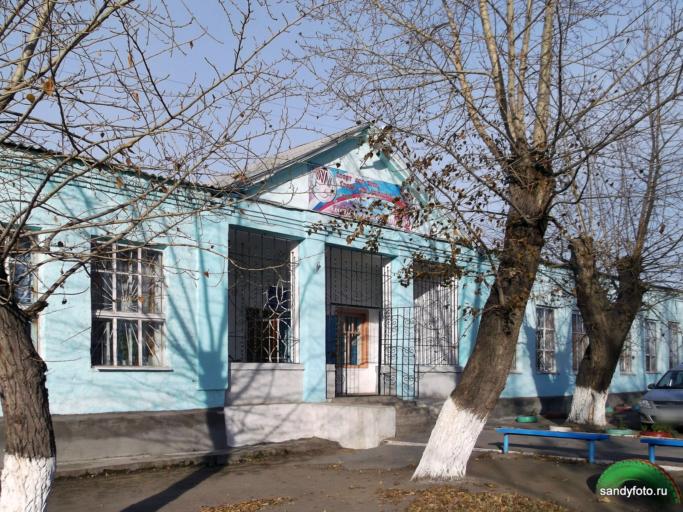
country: RU
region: Chelyabinsk
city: Troitsk
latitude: 54.0959
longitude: 61.5874
